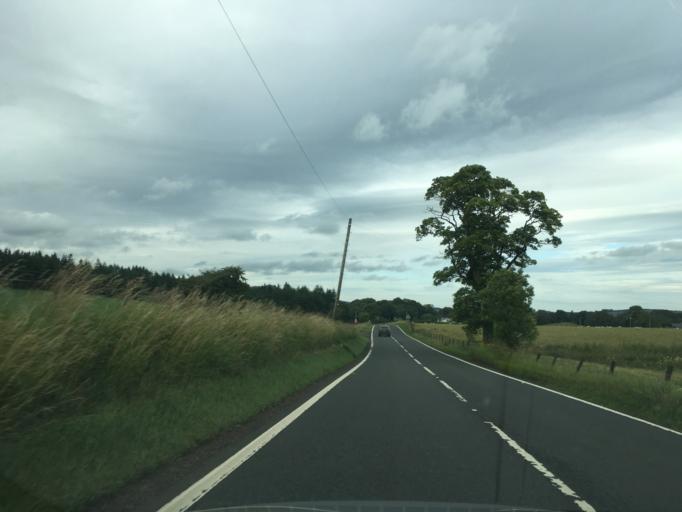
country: GB
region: Scotland
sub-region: The Scottish Borders
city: West Linton
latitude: 55.6942
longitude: -3.4410
